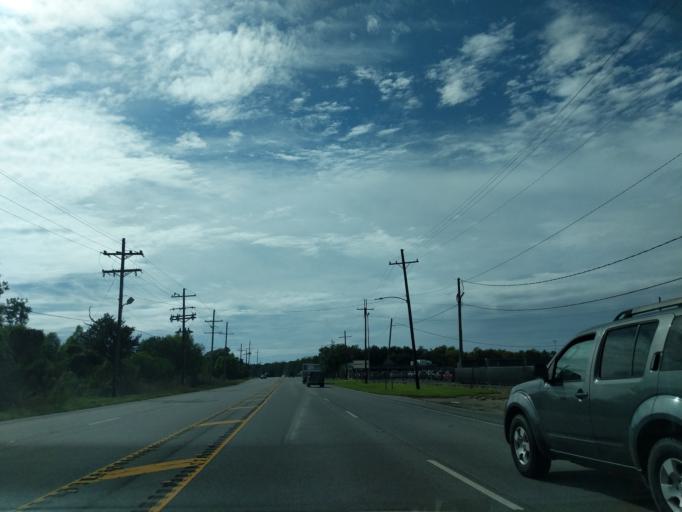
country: US
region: Louisiana
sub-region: Saint Tammany Parish
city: Eden Isle
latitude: 30.0767
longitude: -89.8526
